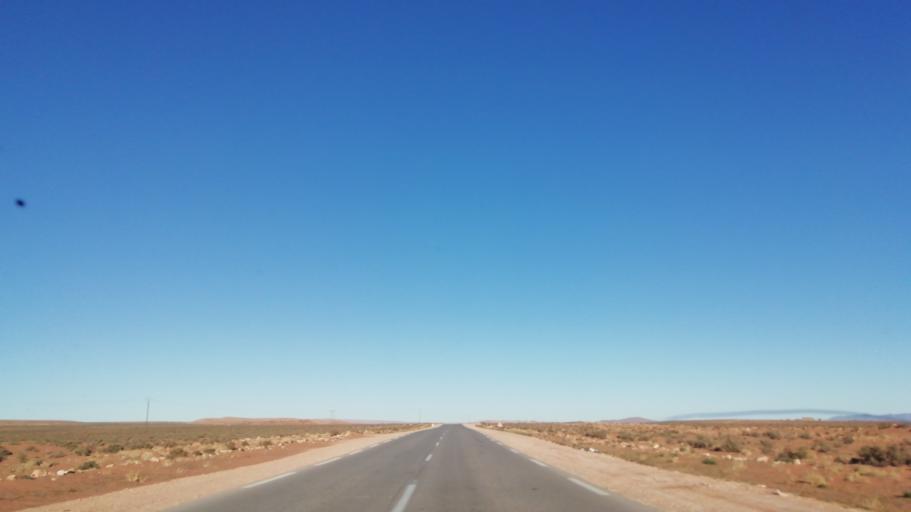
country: DZ
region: El Bayadh
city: El Abiodh Sidi Cheikh
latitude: 33.1260
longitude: 0.2820
